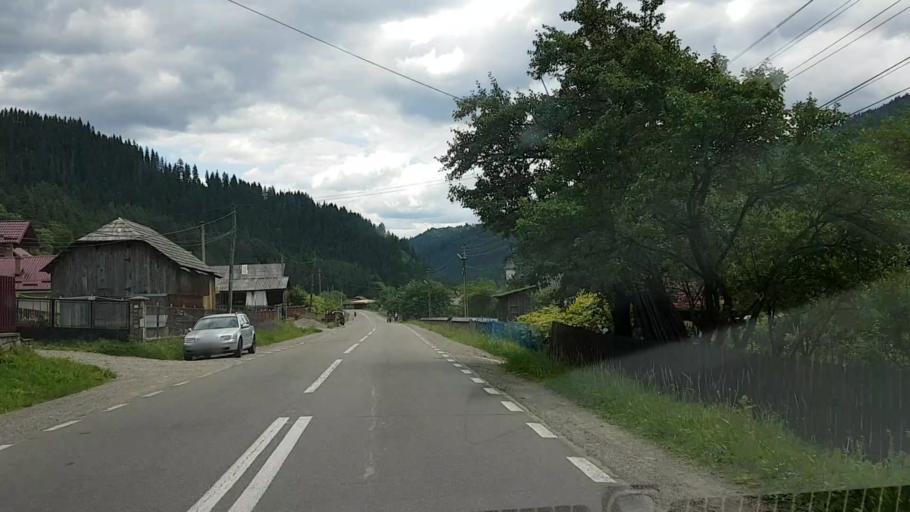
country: RO
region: Neamt
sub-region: Comuna Poiana Teiului
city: Poiana Teiului
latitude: 47.1302
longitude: 25.9009
